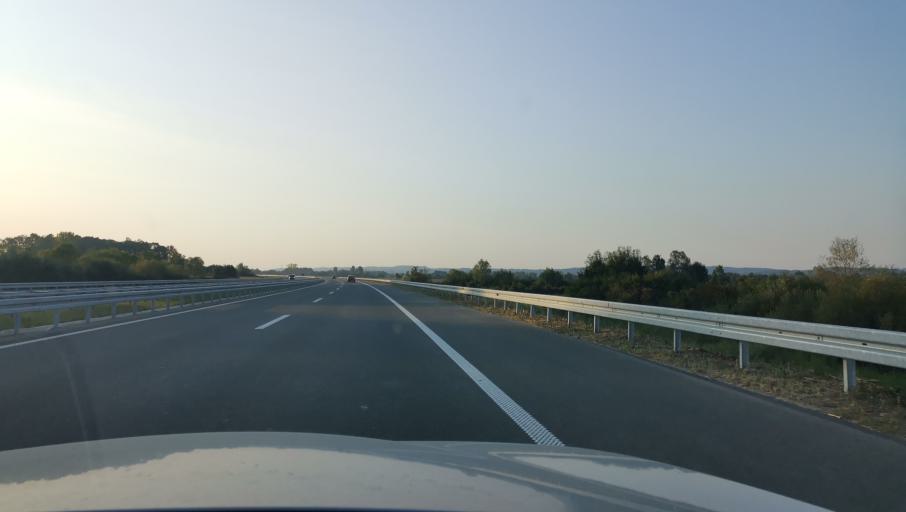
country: RS
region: Central Serbia
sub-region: Kolubarski Okrug
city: Ljig
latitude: 44.2733
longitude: 20.2668
